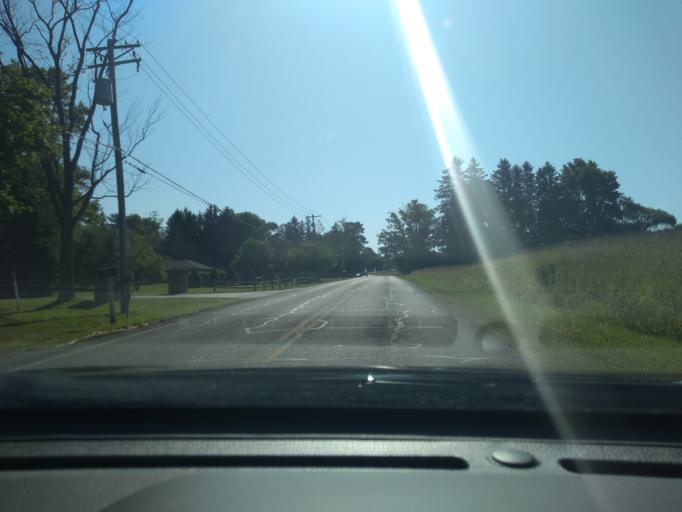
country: US
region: New York
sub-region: Erie County
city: Billington Heights
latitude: 42.7775
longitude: -78.6534
